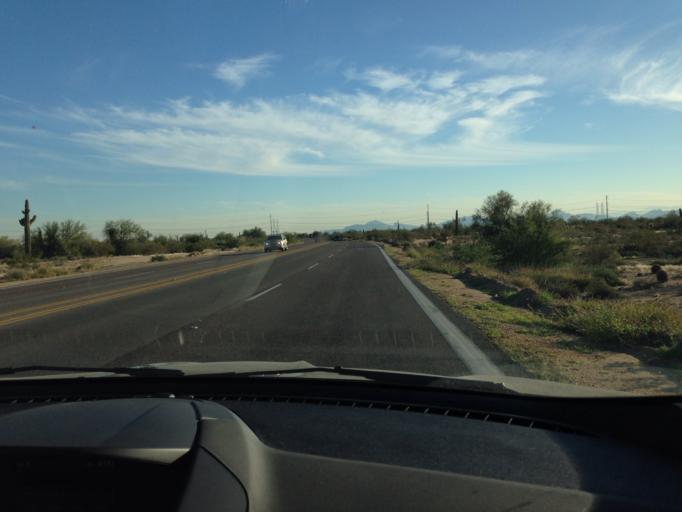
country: US
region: Arizona
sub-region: Maricopa County
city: Cave Creek
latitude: 33.7199
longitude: -111.9775
